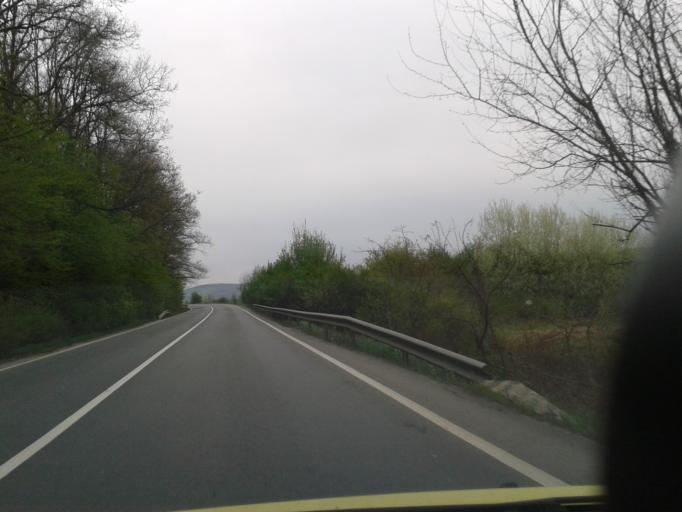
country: RO
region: Arad
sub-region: Comuna Conop
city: Conop
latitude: 46.1118
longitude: 21.8480
